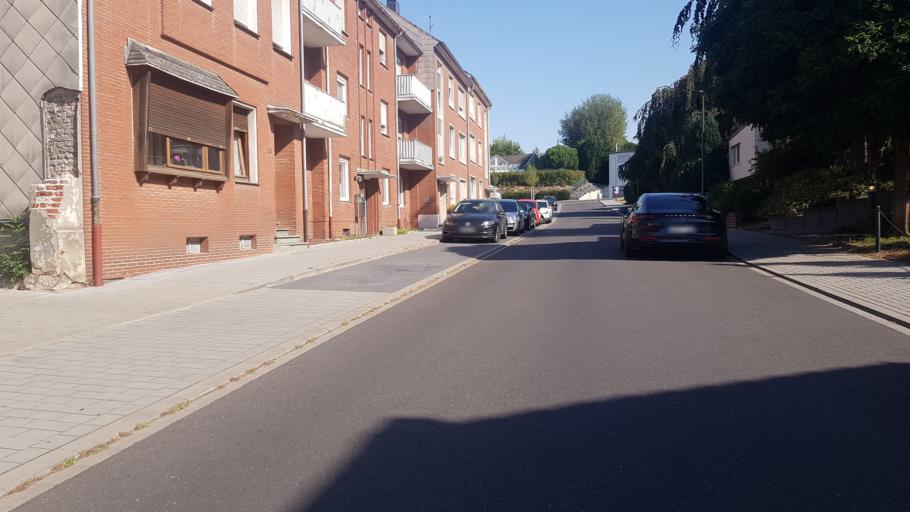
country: DE
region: North Rhine-Westphalia
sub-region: Regierungsbezirk Koln
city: Eschweiler
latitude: 50.8236
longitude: 6.2572
